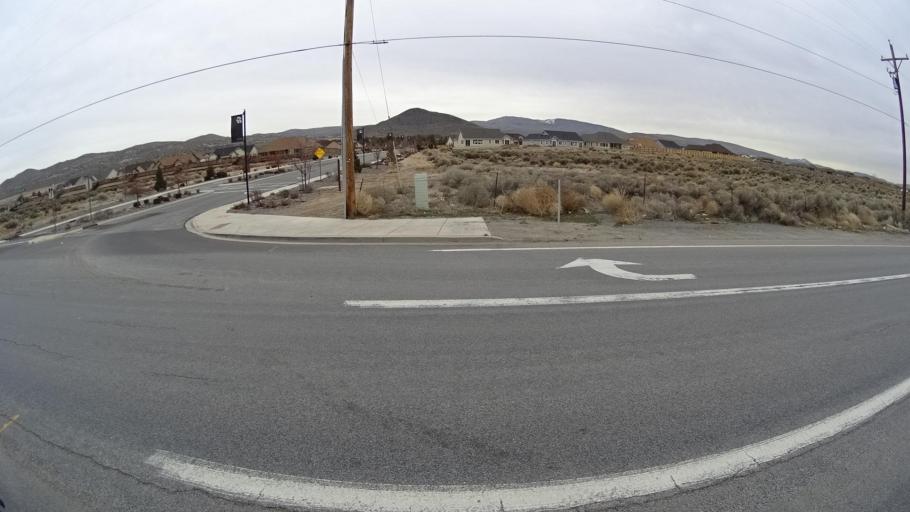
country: US
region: Nevada
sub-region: Washoe County
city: Spanish Springs
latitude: 39.6771
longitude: -119.7009
